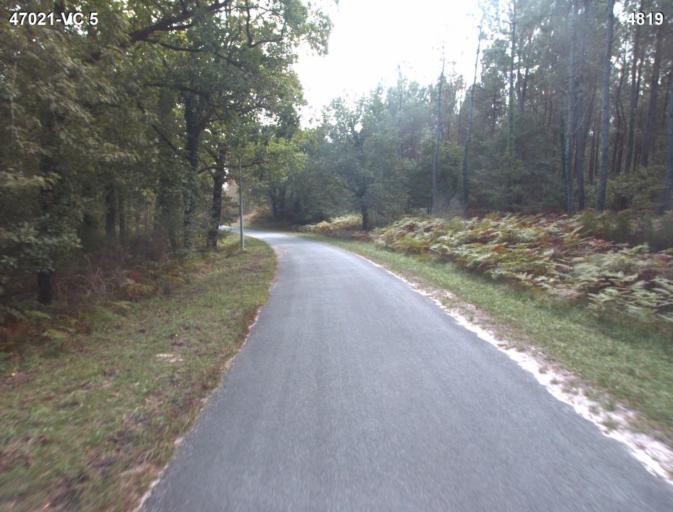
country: FR
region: Aquitaine
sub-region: Departement du Lot-et-Garonne
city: Barbaste
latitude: 44.1459
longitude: 0.2402
